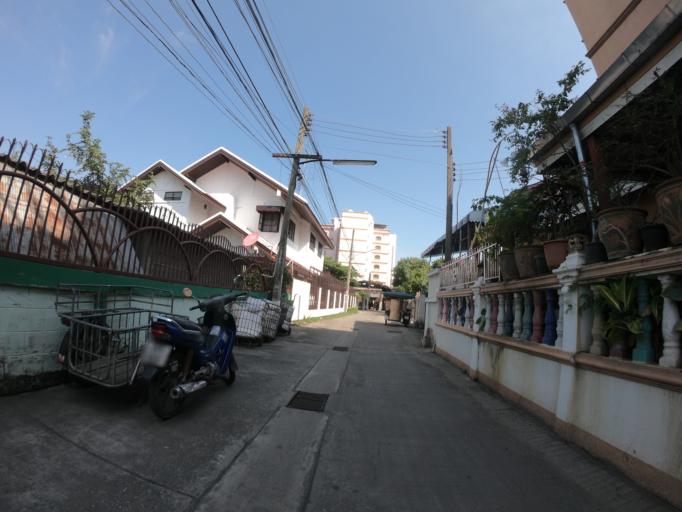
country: TH
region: Chiang Mai
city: Chiang Mai
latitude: 18.7995
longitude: 98.9997
